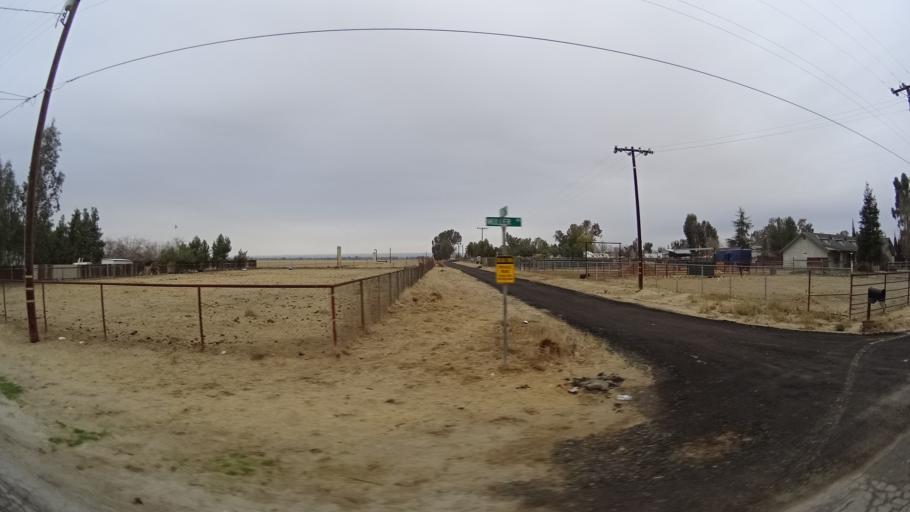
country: US
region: California
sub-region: Kern County
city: Lamont
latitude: 35.3251
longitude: -118.9365
